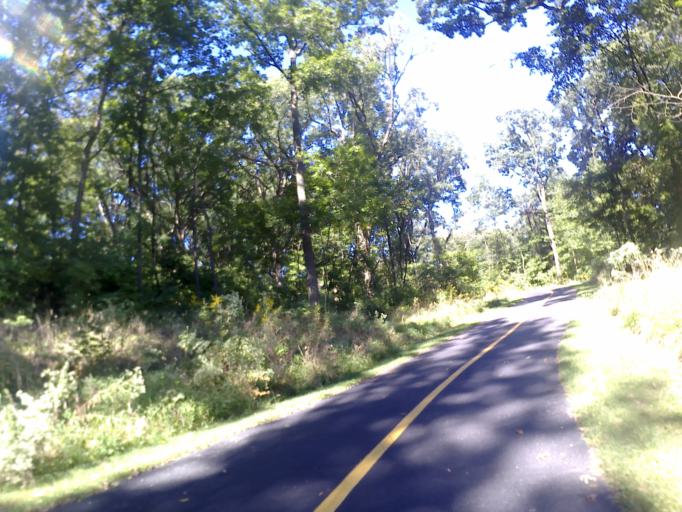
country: US
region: Illinois
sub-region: Cook County
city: Lemont
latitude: 41.6813
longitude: -88.0299
